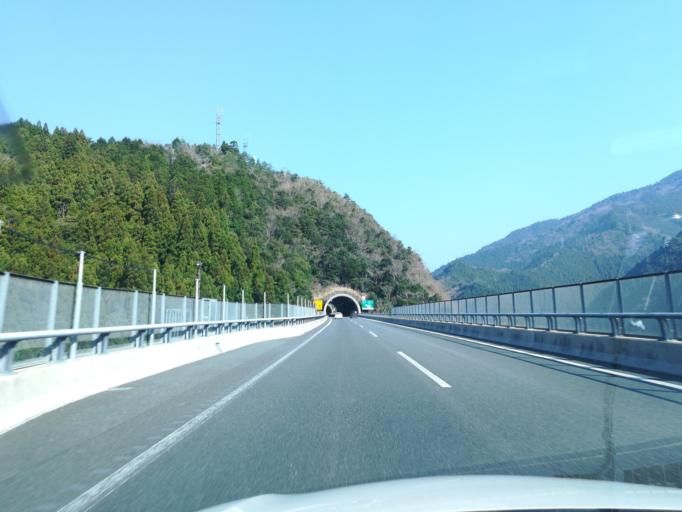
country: JP
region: Ehime
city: Kawanoecho
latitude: 33.8244
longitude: 133.6620
